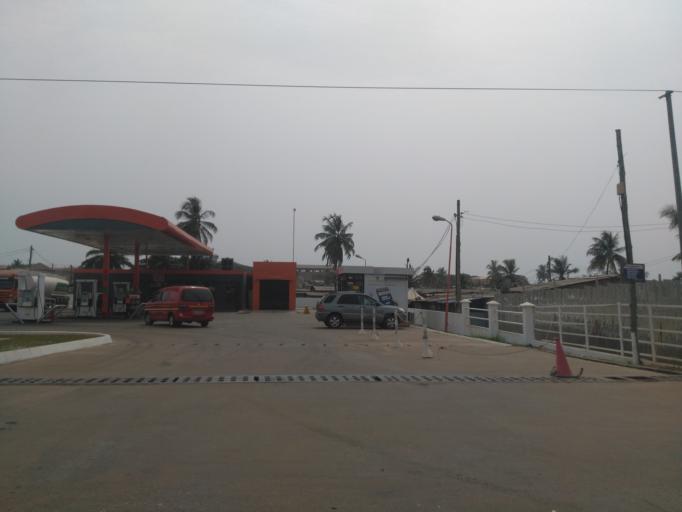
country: GH
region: Greater Accra
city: Nungua
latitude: 5.5978
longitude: -0.0823
